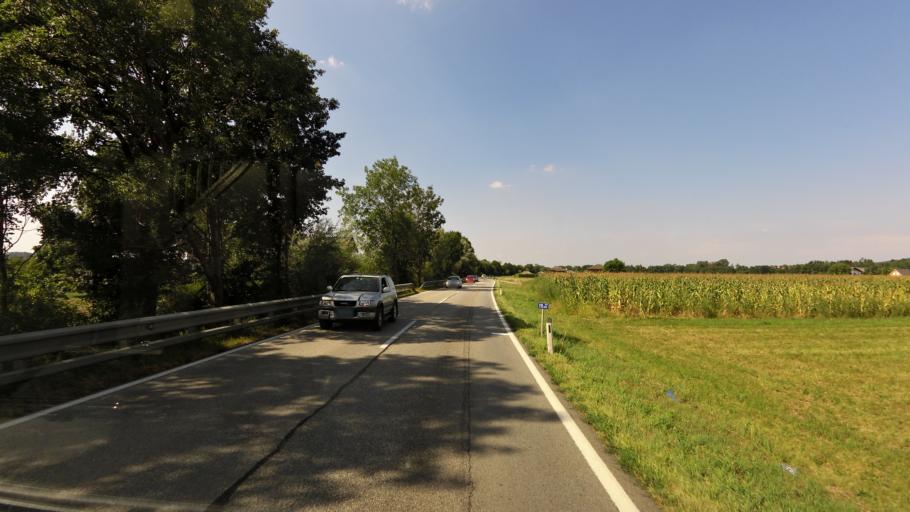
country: AT
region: Upper Austria
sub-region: Politischer Bezirk Braunau am Inn
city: Altheim
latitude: 48.1233
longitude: 13.1500
